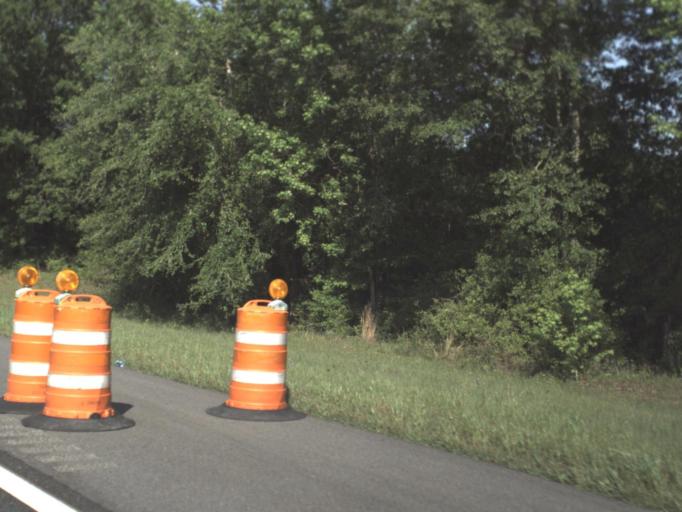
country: US
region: Florida
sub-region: Walton County
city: DeFuniak Springs
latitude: 30.7199
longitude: -85.9211
